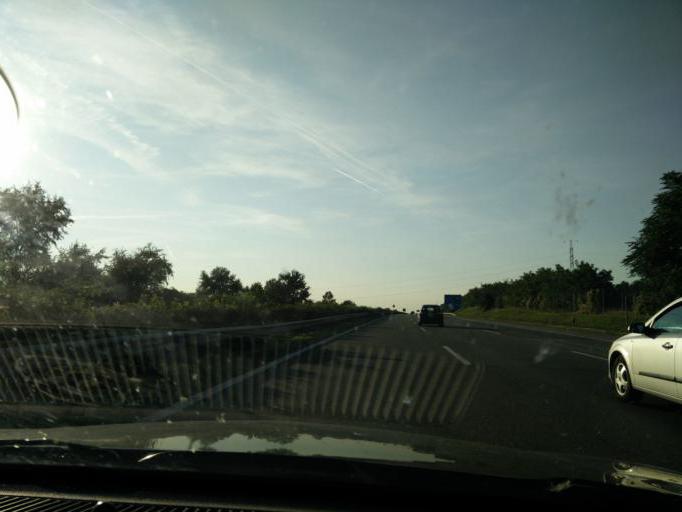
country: HU
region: Pest
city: Biatorbagy
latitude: 47.4755
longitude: 18.8512
